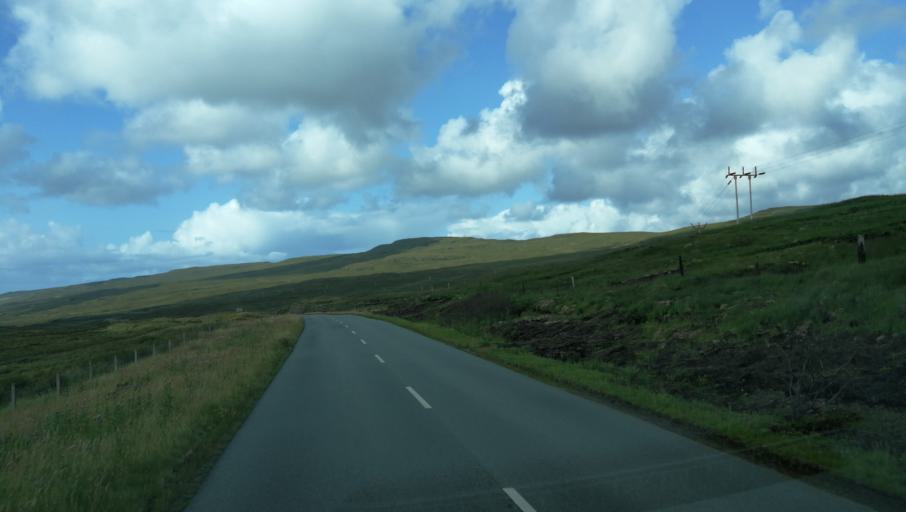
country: GB
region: Scotland
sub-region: Highland
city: Isle of Skye
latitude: 57.4640
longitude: -6.5423
